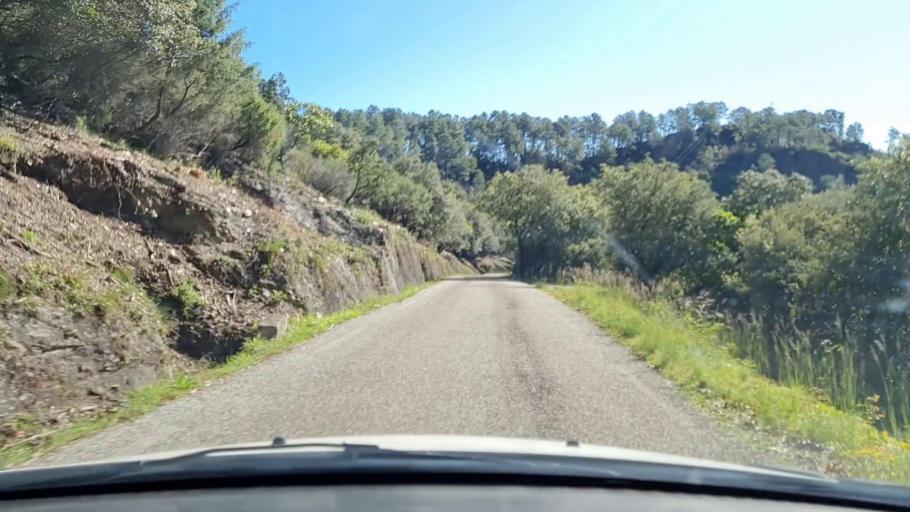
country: FR
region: Languedoc-Roussillon
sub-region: Departement du Gard
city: Branoux-les-Taillades
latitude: 44.1857
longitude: 3.9915
